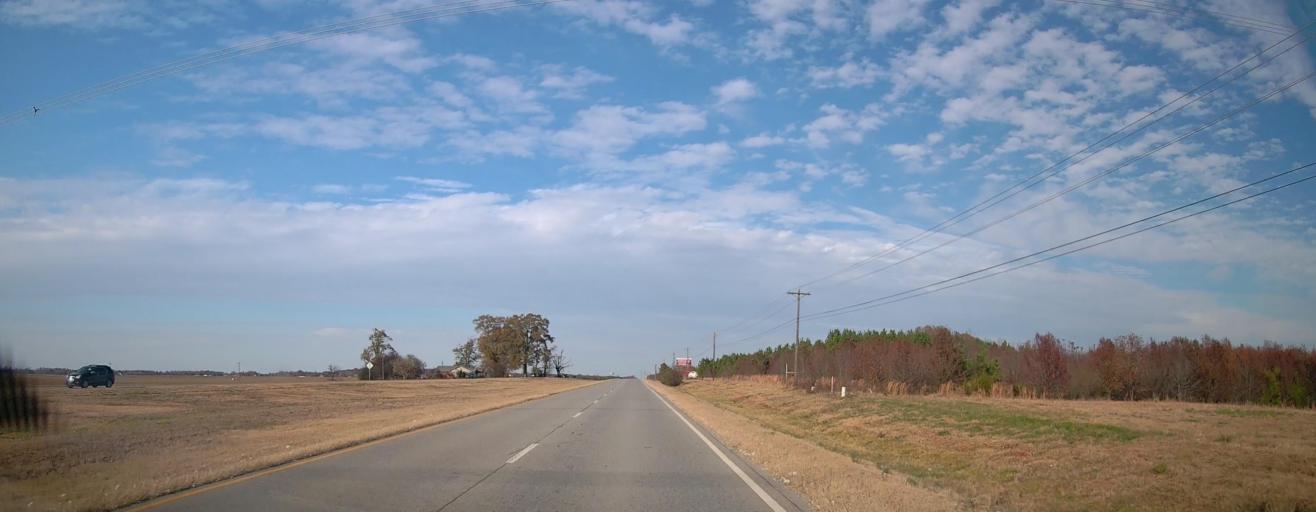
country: US
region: Alabama
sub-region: Morgan County
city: Decatur
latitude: 34.6957
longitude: -86.9555
